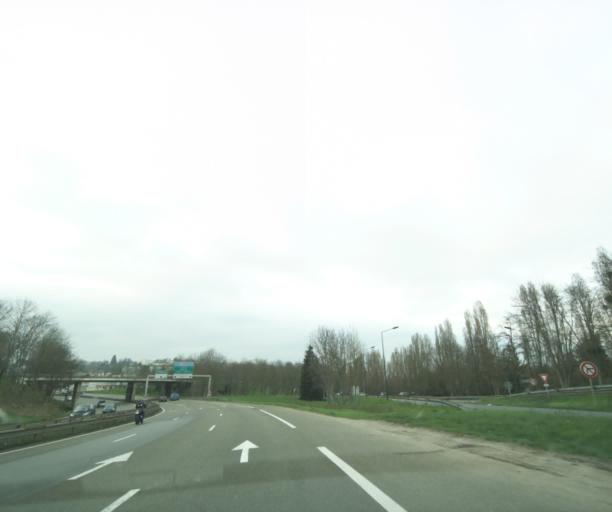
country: FR
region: Ile-de-France
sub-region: Departement des Yvelines
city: Le Port-Marly
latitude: 48.8855
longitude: 2.1057
